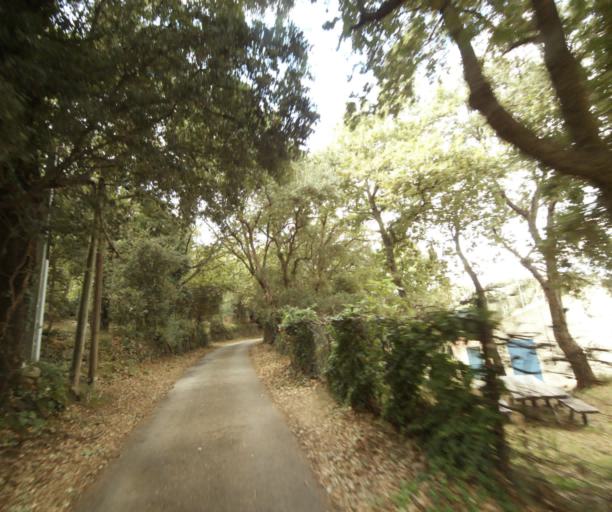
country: FR
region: Languedoc-Roussillon
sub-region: Departement des Pyrenees-Orientales
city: Argelers
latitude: 42.5289
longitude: 3.0042
